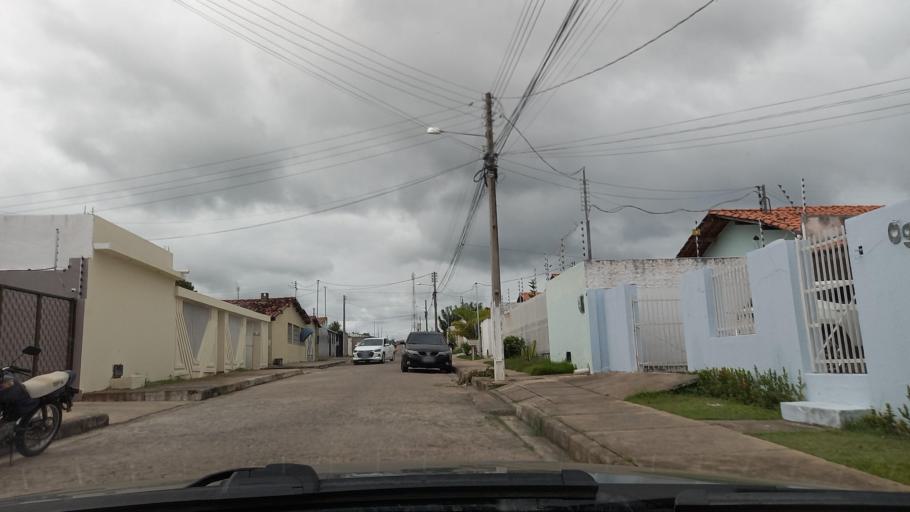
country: BR
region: Sergipe
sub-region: Caninde De Sao Francisco
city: Caninde de Sao Francisco
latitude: -9.6090
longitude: -37.7665
